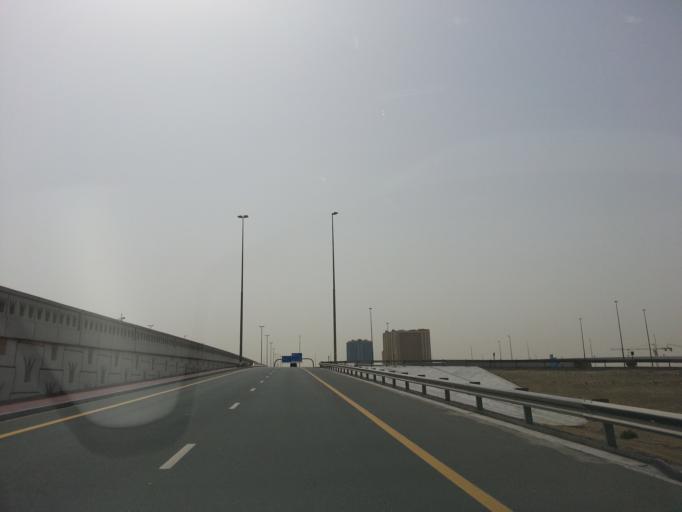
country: AE
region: Dubai
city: Dubai
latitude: 25.0454
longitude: 55.1980
